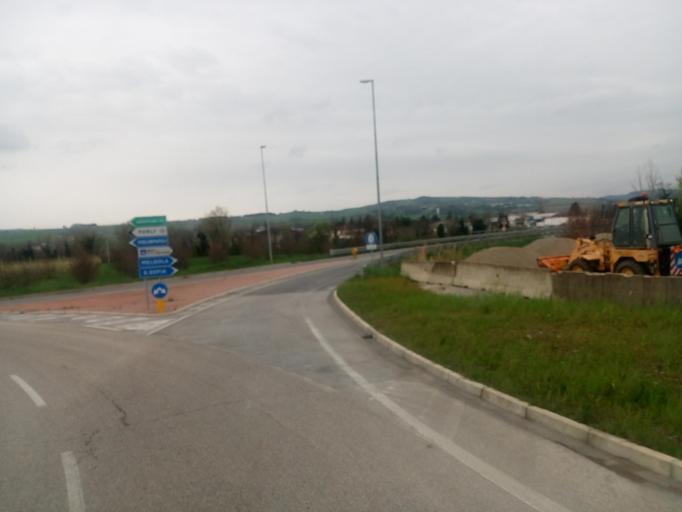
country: IT
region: Emilia-Romagna
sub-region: Forli-Cesena
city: Meldola
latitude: 44.1465
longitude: 12.0714
